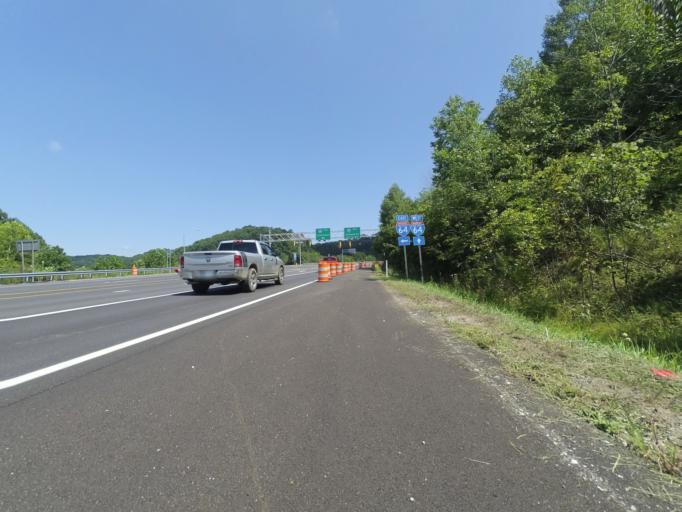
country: US
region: West Virginia
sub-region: Cabell County
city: Huntington
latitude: 38.3915
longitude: -82.4538
